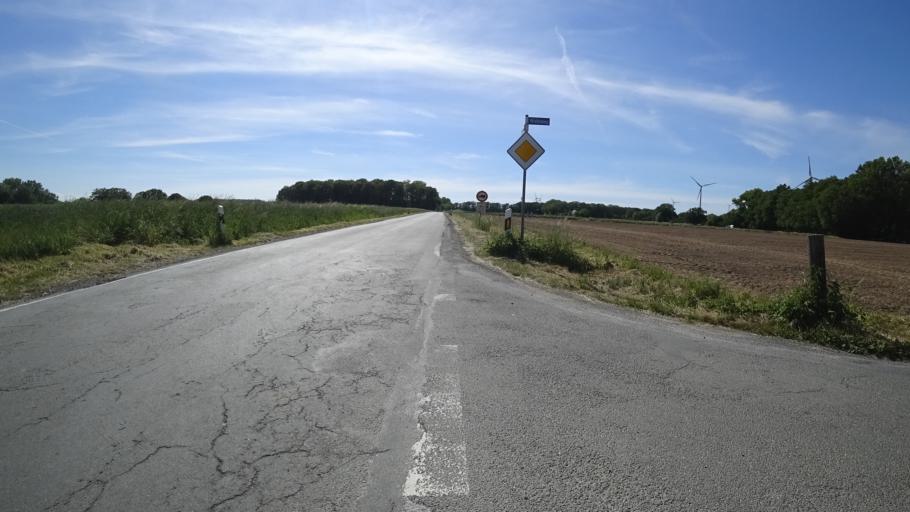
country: DE
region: North Rhine-Westphalia
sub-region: Regierungsbezirk Detmold
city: Rheda-Wiedenbruck
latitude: 51.8239
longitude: 8.2606
